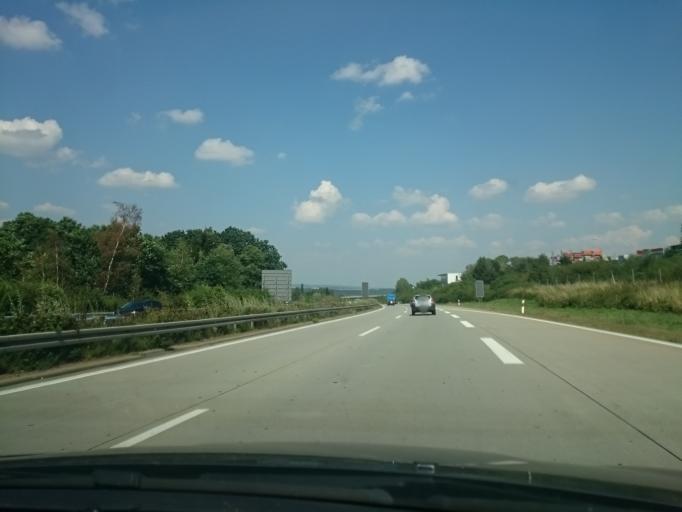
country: DE
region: Saxony
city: Stollberg
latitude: 50.7072
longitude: 12.7563
